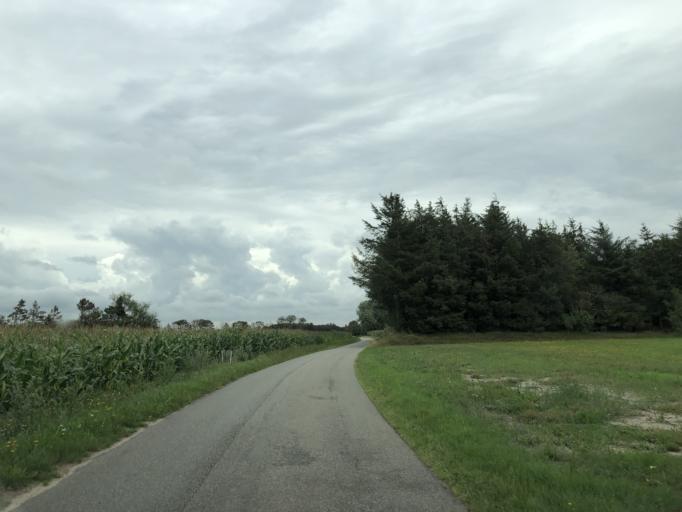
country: DK
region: Central Jutland
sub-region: Ringkobing-Skjern Kommune
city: Ringkobing
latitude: 56.1306
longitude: 8.2636
